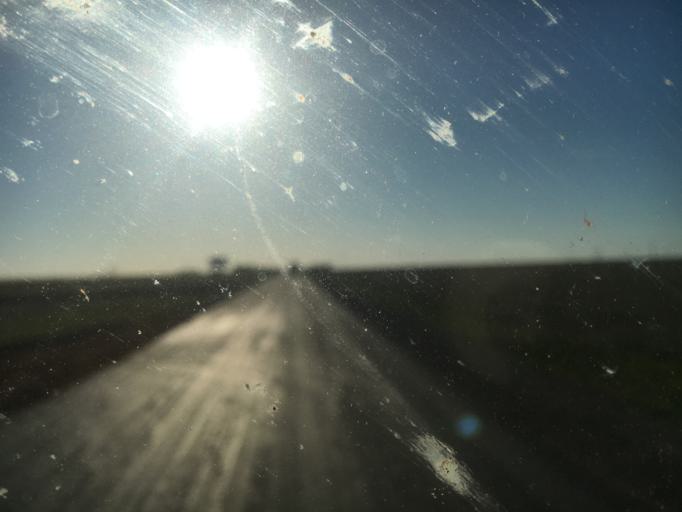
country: KZ
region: Aqtoebe
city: Batamshinskiy
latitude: 50.2485
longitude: 57.9881
